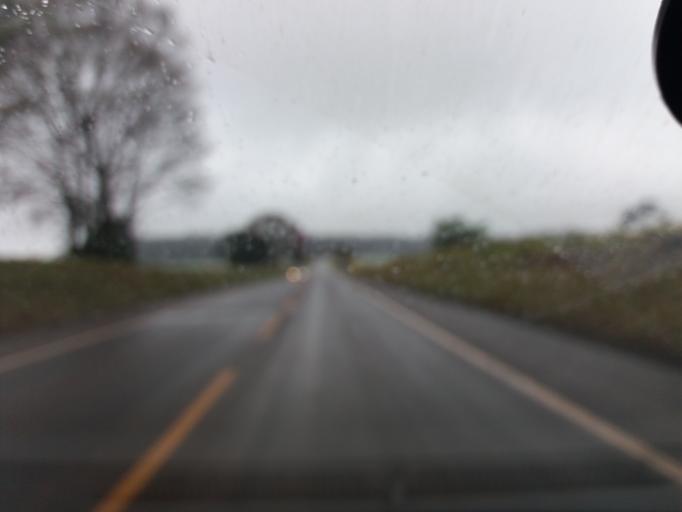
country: BR
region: Parana
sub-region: Campo Mourao
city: Campo Mourao
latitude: -24.2942
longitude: -52.5827
